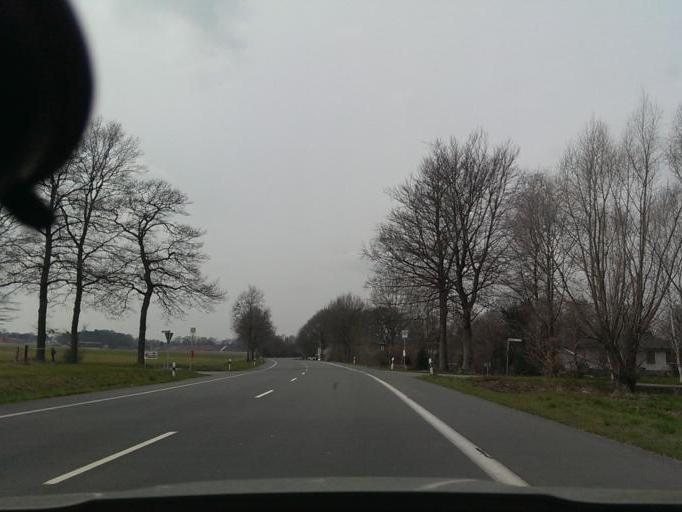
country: DE
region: North Rhine-Westphalia
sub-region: Regierungsbezirk Detmold
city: Delbruck
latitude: 51.7591
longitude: 8.5003
